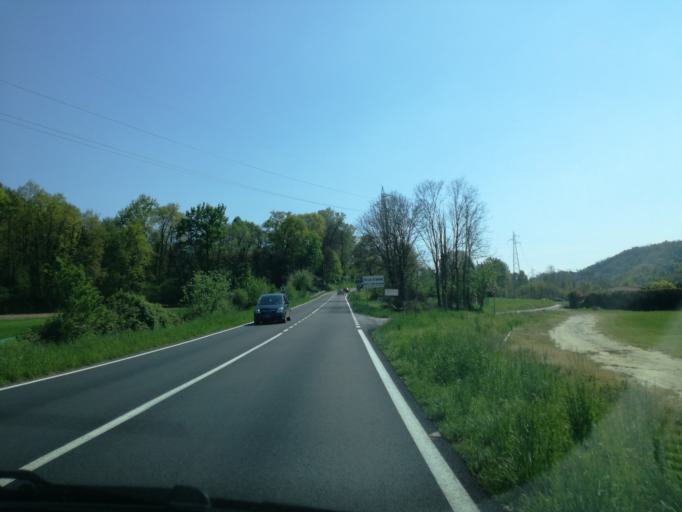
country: IT
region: Lombardy
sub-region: Provincia di Lecco
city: Arlate
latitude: 45.7292
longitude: 9.4530
